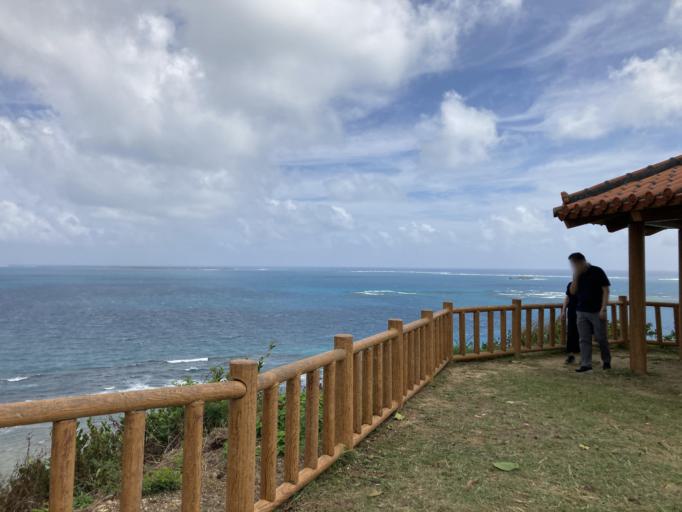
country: JP
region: Okinawa
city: Ginowan
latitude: 26.1676
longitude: 127.8293
